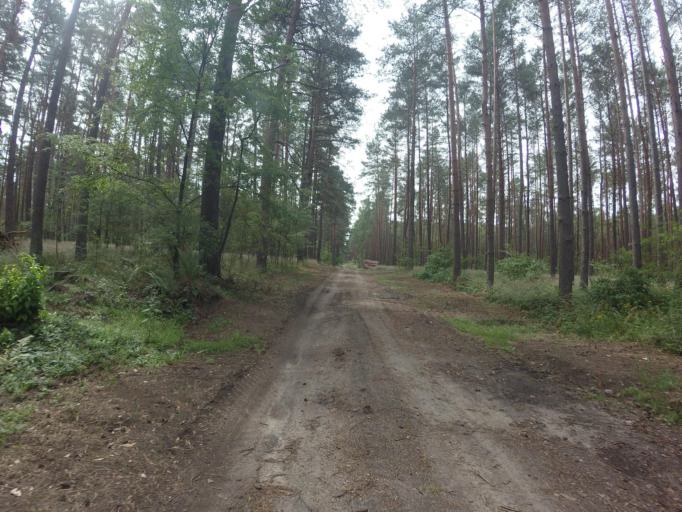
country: PL
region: West Pomeranian Voivodeship
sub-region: Powiat choszczenski
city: Bierzwnik
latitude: 53.1247
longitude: 15.6870
